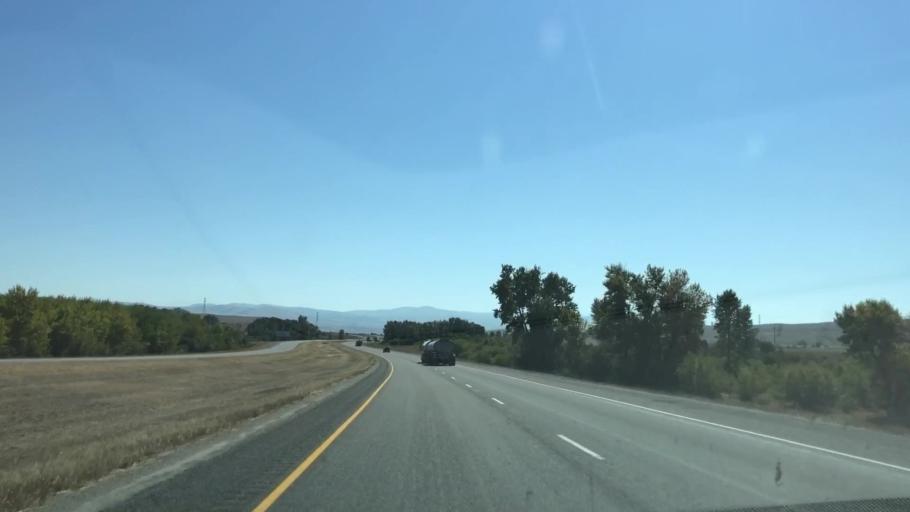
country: US
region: Montana
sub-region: Powell County
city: Deer Lodge
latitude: 46.5203
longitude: -112.8052
